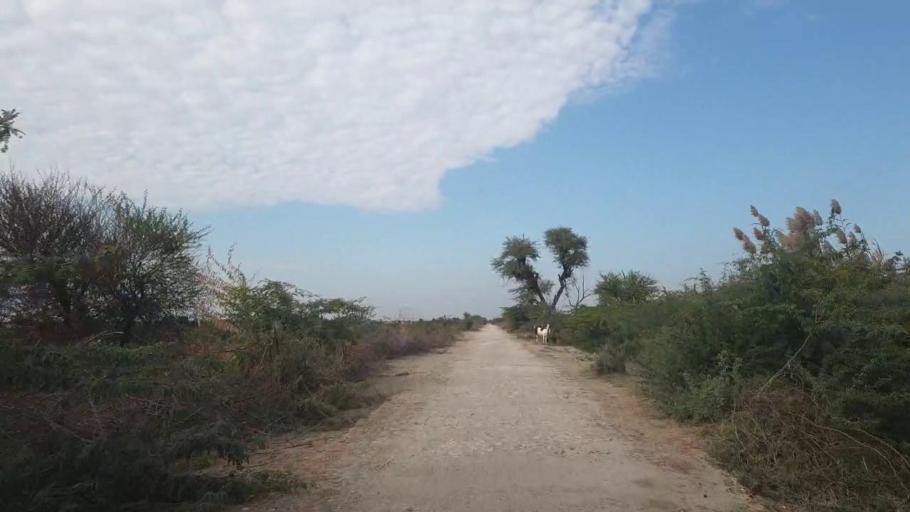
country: PK
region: Sindh
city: Sinjhoro
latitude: 26.0529
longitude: 68.8751
